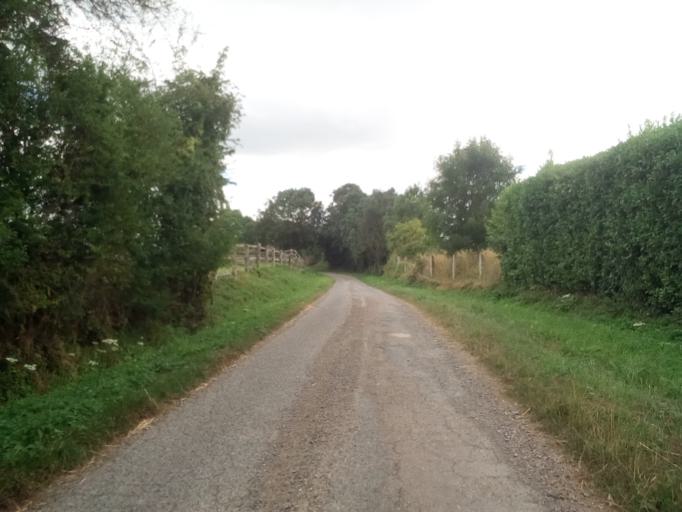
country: FR
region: Lower Normandy
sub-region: Departement du Calvados
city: Troarn
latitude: 49.1704
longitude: -0.1425
